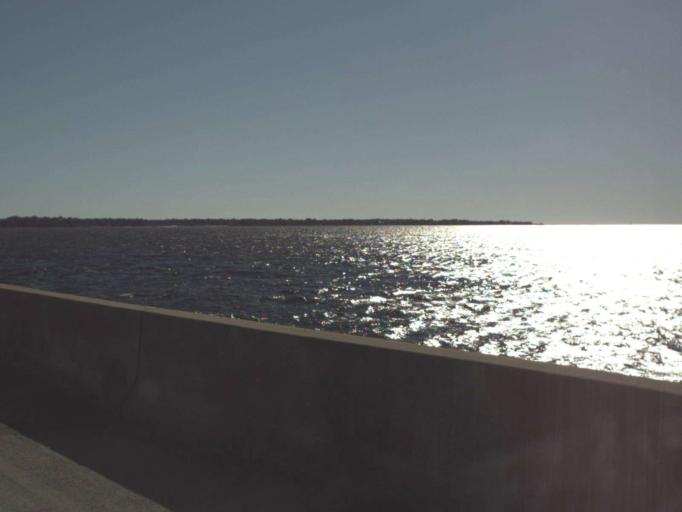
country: US
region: Florida
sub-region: Santa Rosa County
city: Gulf Breeze
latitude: 30.3903
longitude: -87.1835
